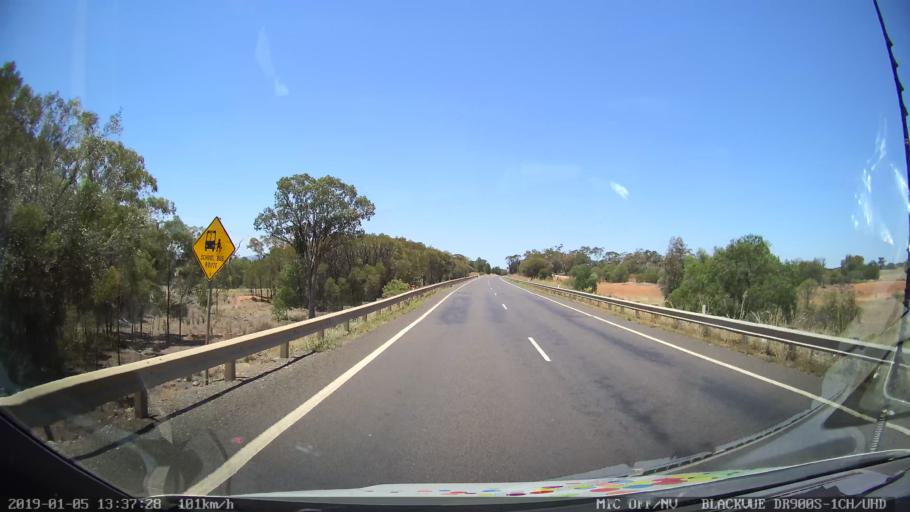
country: AU
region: New South Wales
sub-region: Gunnedah
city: Gunnedah
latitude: -30.9818
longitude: 150.1824
